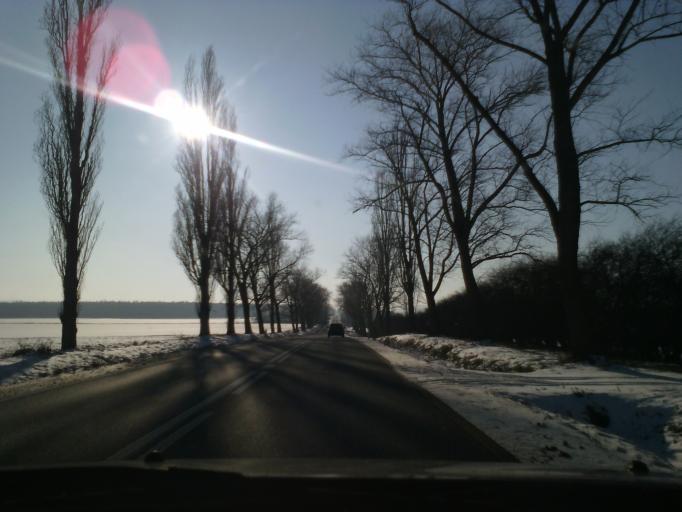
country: PL
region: Lower Silesian Voivodeship
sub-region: Powiat swidnicki
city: Stanowice
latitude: 50.9115
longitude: 16.3648
